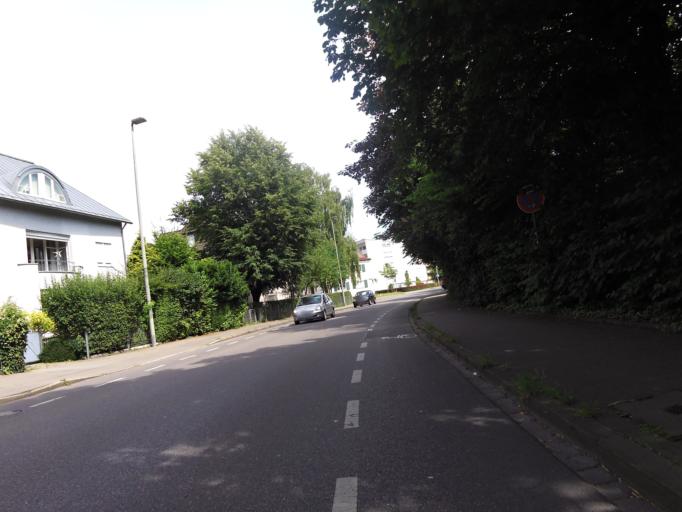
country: DE
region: Baden-Wuerttemberg
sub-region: Tuebingen Region
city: Friedrichshafen
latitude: 47.6524
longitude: 9.4911
